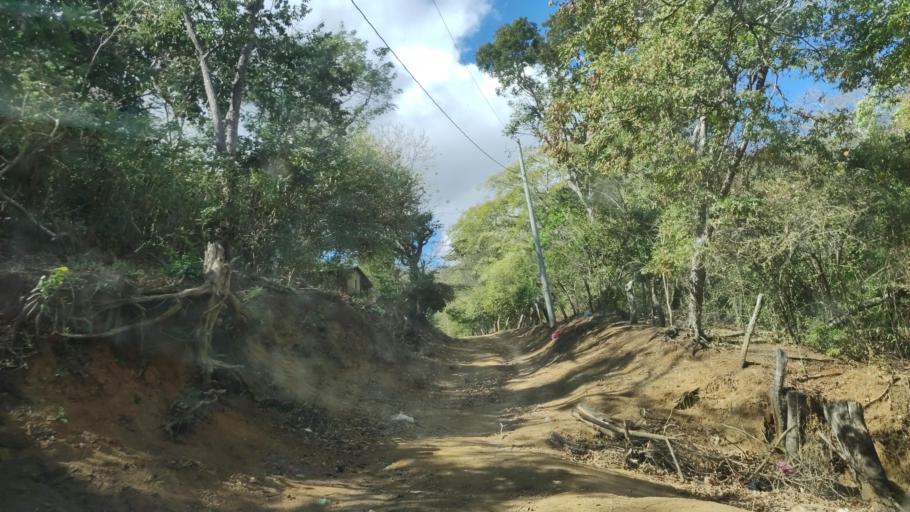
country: NI
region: Carazo
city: Santa Teresa
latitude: 11.6537
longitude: -86.1966
